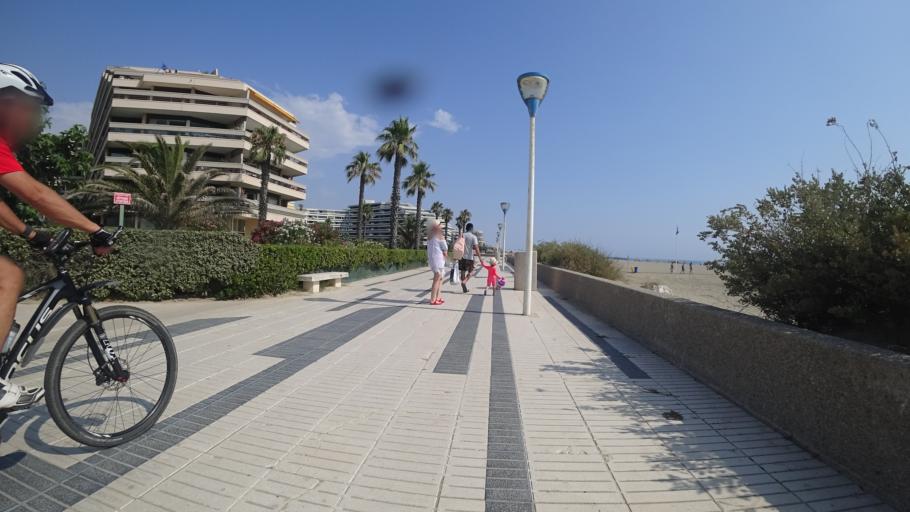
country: FR
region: Languedoc-Roussillon
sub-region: Departement des Pyrenees-Orientales
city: Canet-en-Roussillon
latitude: 42.6755
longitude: 3.0339
